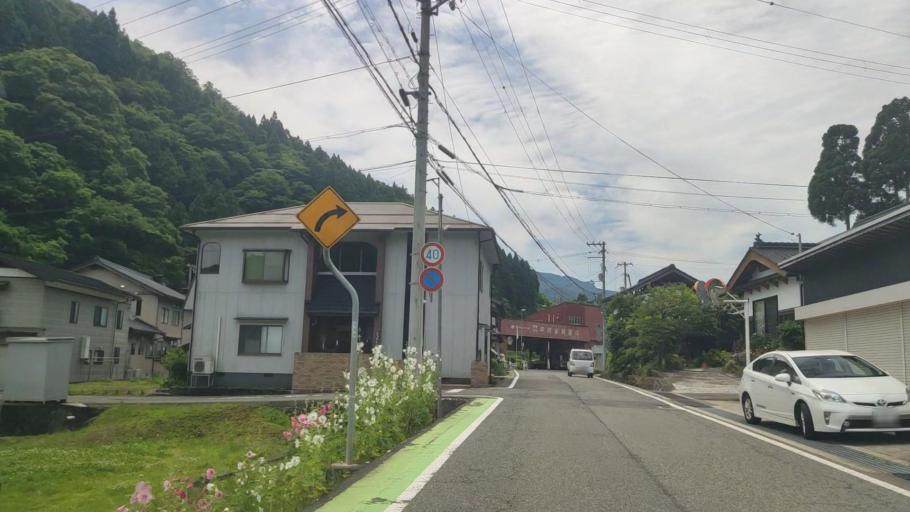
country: JP
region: Hyogo
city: Toyooka
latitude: 35.4851
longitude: 134.5533
